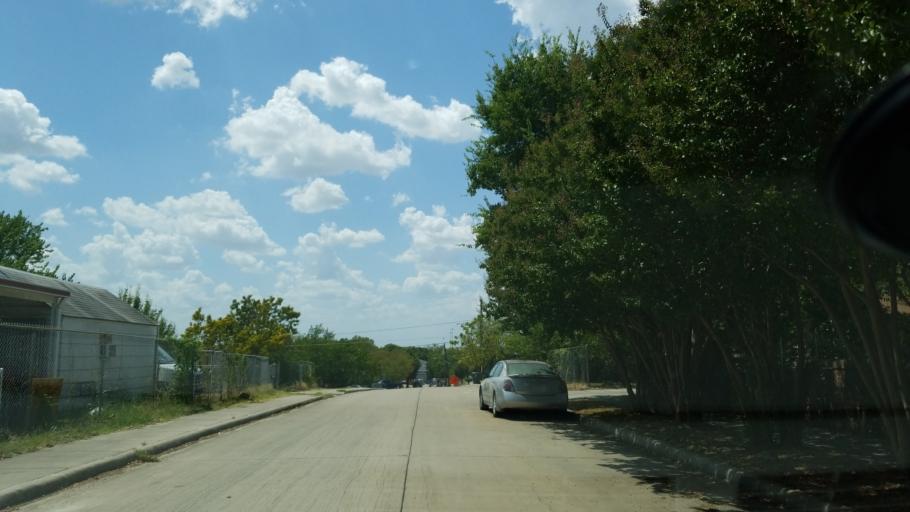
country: US
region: Texas
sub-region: Dallas County
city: Cockrell Hill
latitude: 32.7469
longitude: -96.9090
